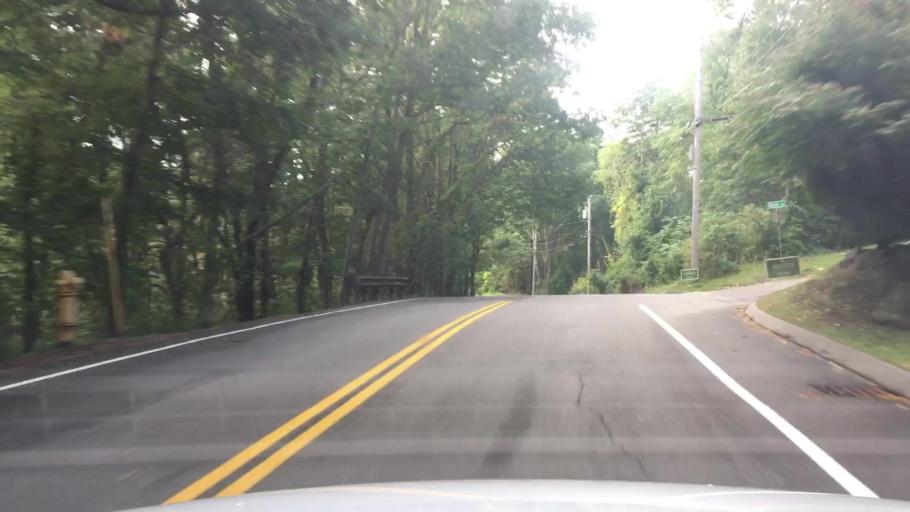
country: US
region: Maine
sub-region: York County
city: Kittery Point
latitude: 43.0864
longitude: -70.7113
